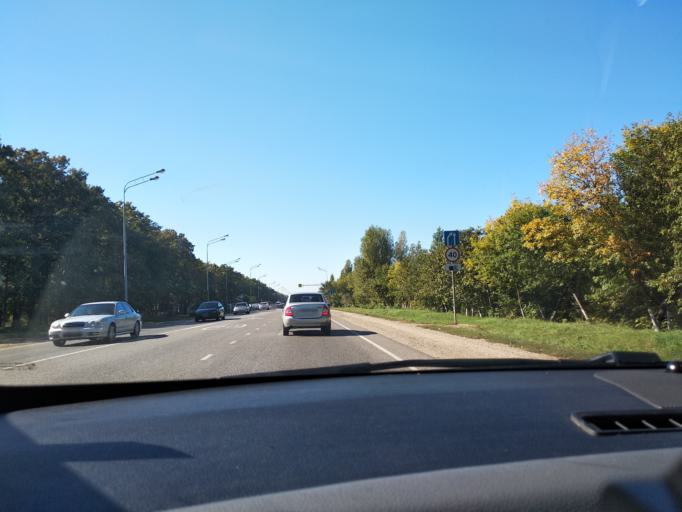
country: RU
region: Krasnodarskiy
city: Novotitarovskaya
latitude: 45.1444
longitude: 39.0465
